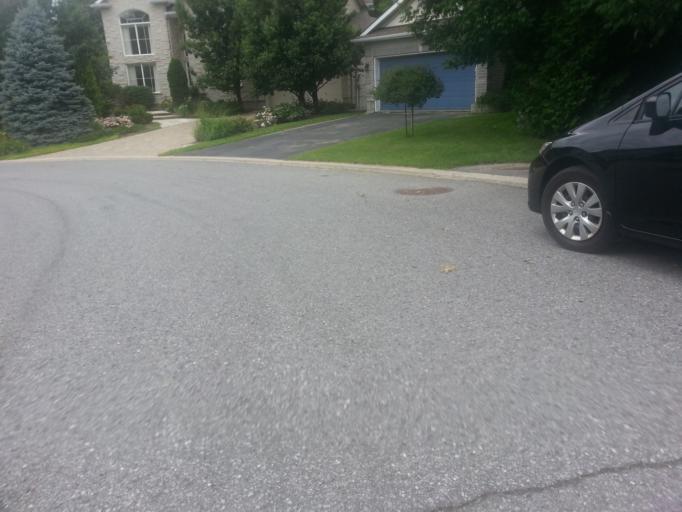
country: CA
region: Ontario
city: Bells Corners
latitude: 45.3303
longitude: -75.9216
